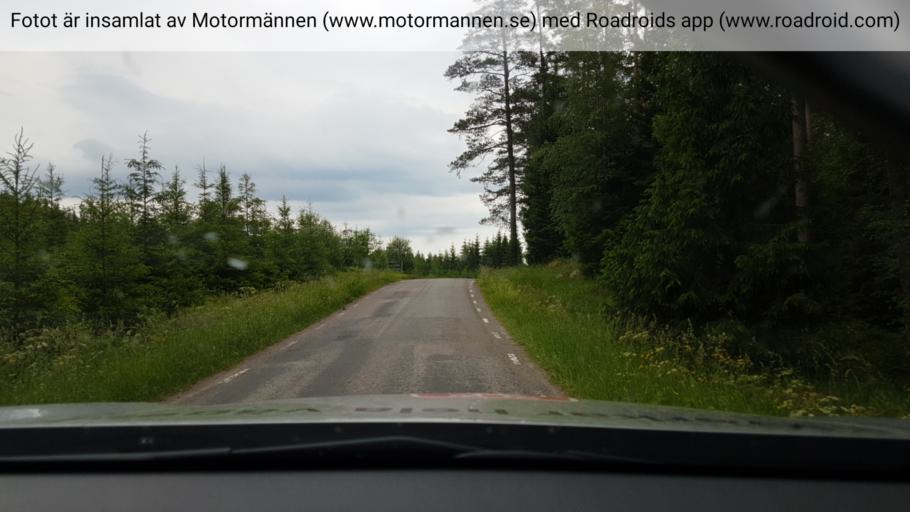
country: SE
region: Joenkoeping
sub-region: Mullsjo Kommun
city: Mullsjoe
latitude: 57.9550
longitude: 13.7061
